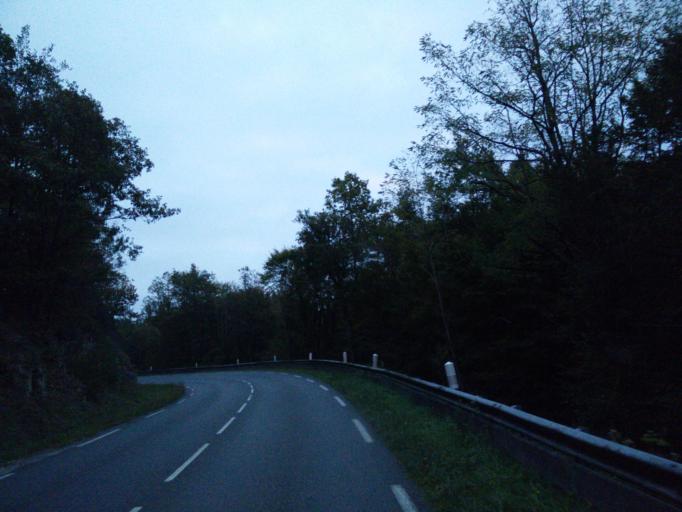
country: FR
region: Aquitaine
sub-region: Departement de la Dordogne
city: Sarlat-la-Caneda
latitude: 44.9117
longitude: 1.1592
